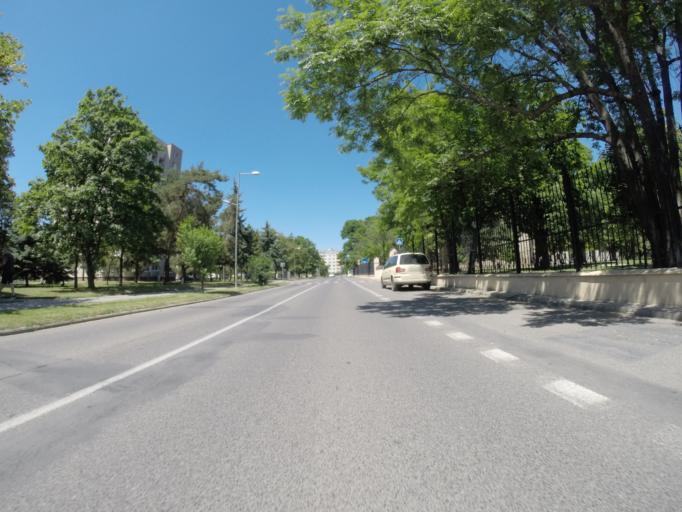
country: SK
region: Trnavsky
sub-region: Okres Galanta
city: Galanta
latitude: 48.1912
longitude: 17.7366
